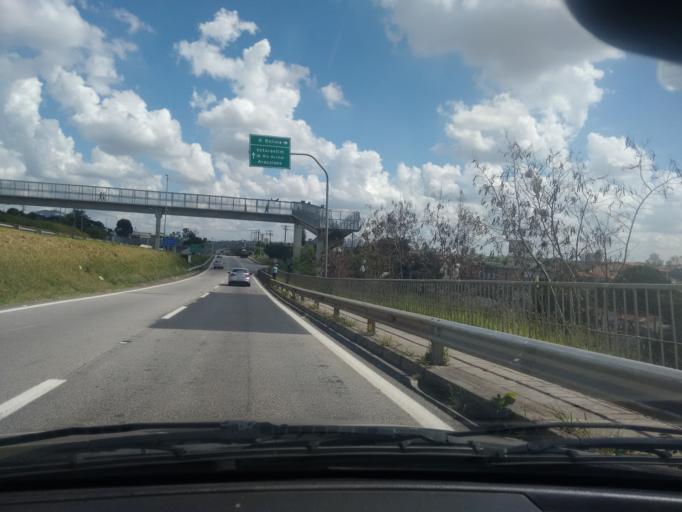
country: BR
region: Sao Paulo
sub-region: Votorantim
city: Votorantim
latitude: -23.5189
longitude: -47.4343
